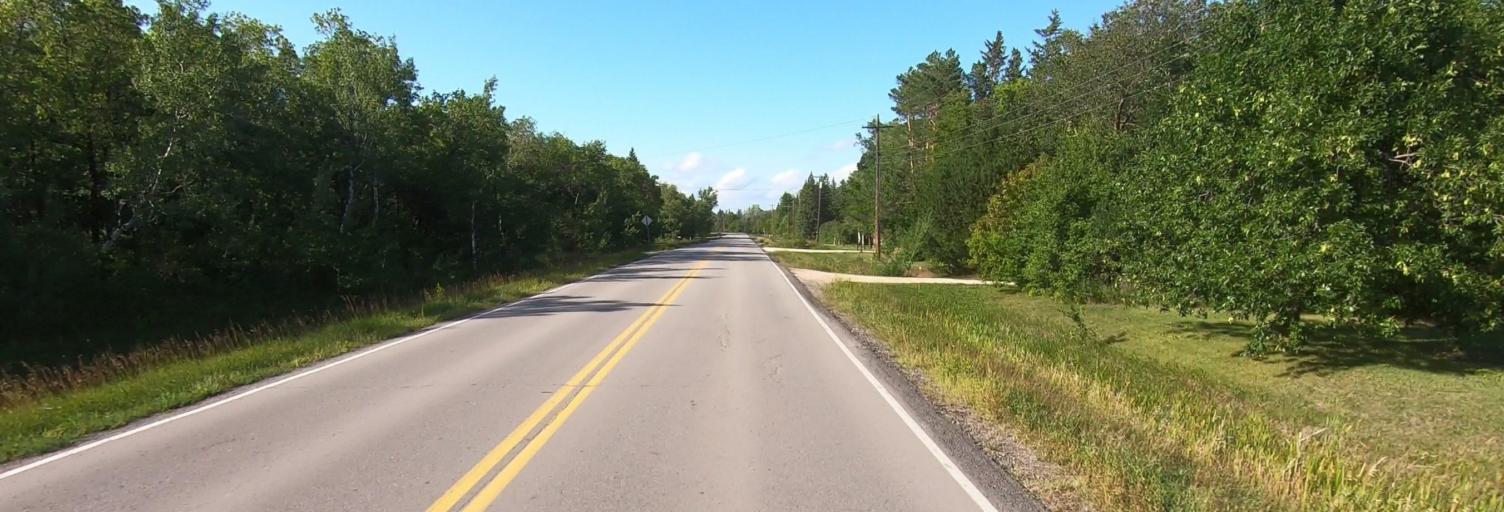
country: CA
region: Manitoba
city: Selkirk
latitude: 50.0971
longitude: -96.9330
